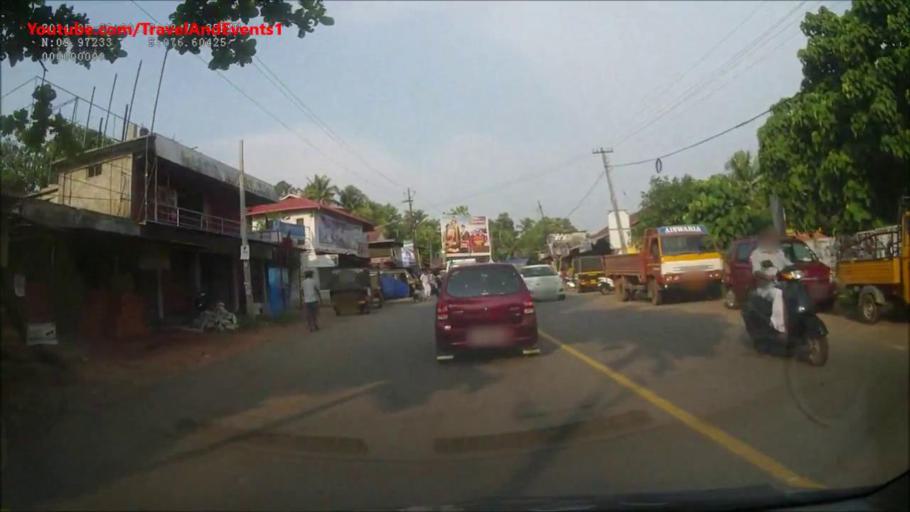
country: IN
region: Kerala
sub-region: Ernakulam
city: Muvattupula
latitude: 9.9649
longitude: 76.6148
